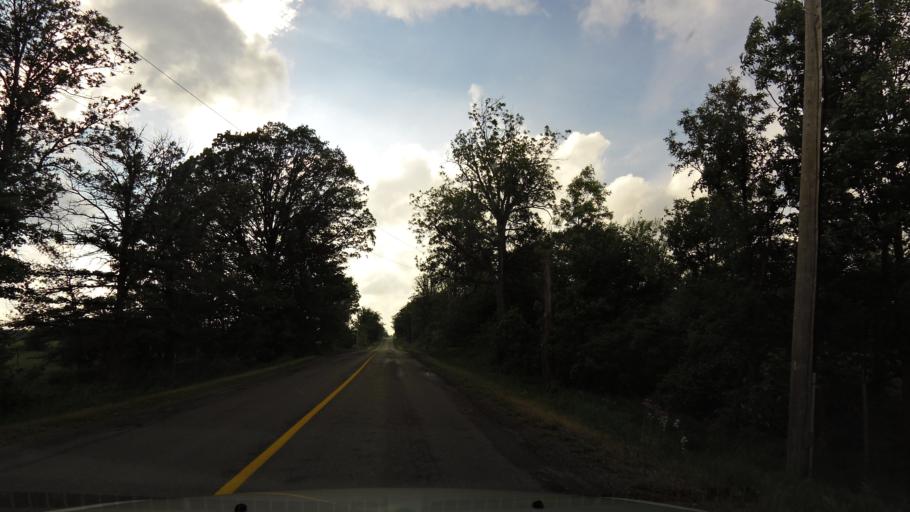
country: CA
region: Ontario
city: Brantford
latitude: 43.0135
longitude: -80.0802
